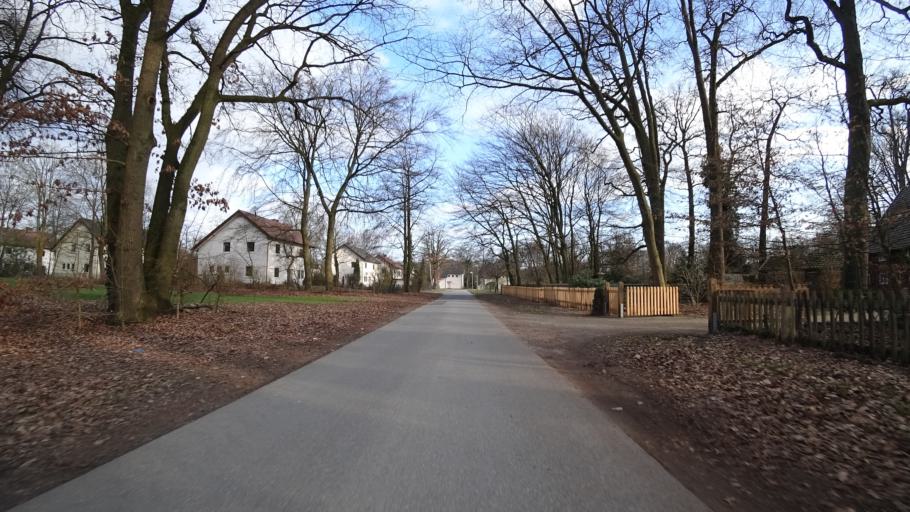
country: DE
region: North Rhine-Westphalia
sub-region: Regierungsbezirk Detmold
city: Guetersloh
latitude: 51.9016
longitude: 8.3928
